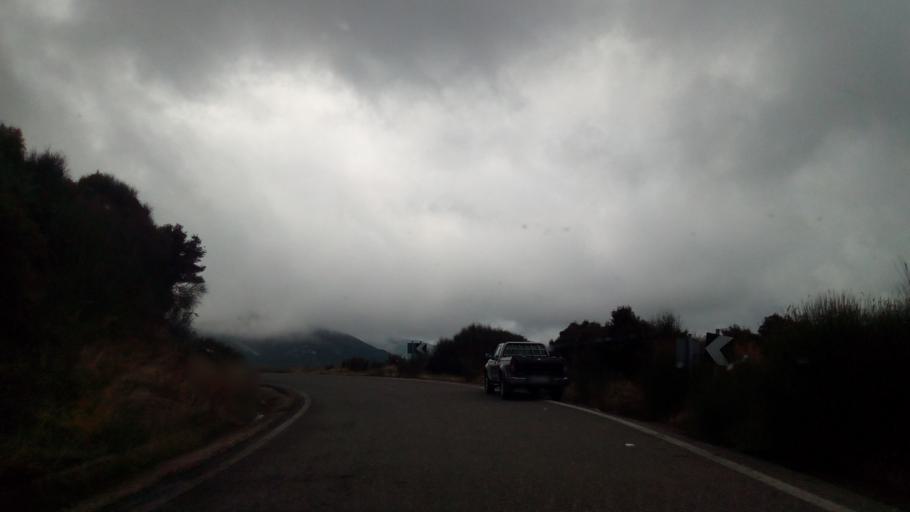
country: GR
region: West Greece
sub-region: Nomos Aitolias kai Akarnanias
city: Nafpaktos
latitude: 38.5137
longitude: 21.8366
